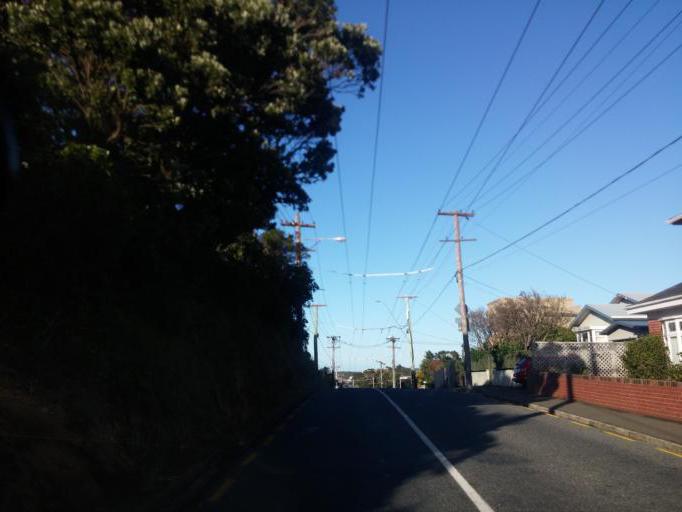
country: NZ
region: Wellington
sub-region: Wellington City
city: Brooklyn
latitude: -41.3104
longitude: 174.7662
